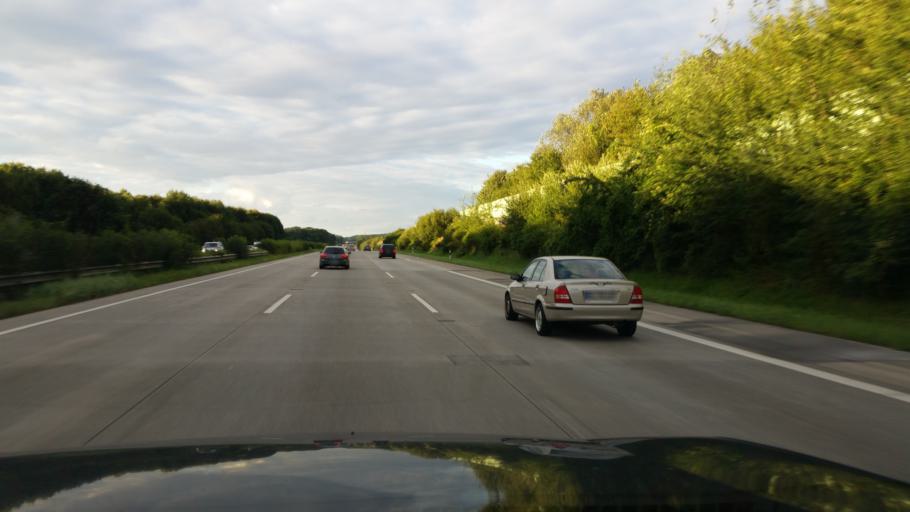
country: DE
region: Schleswig-Holstein
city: Grosshansdorf
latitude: 53.6680
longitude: 10.3046
